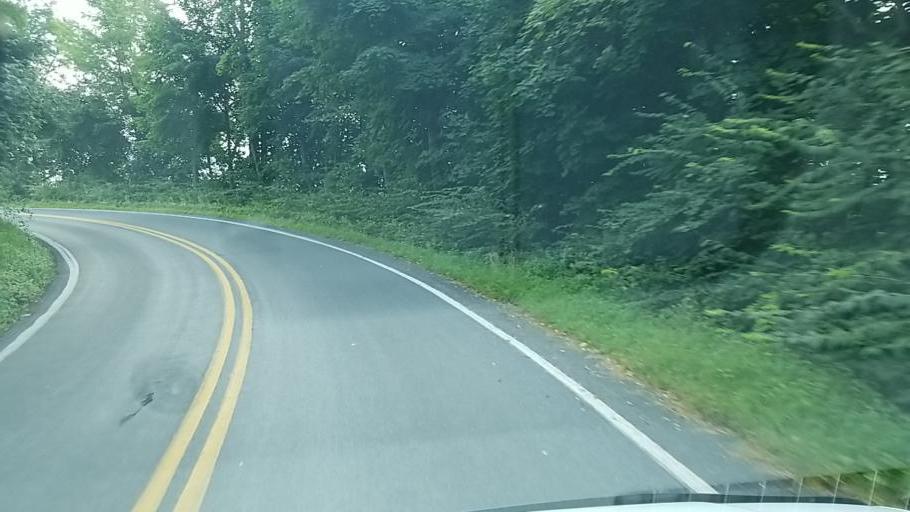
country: US
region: Pennsylvania
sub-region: Dauphin County
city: Millersburg
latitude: 40.5619
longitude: -76.8940
